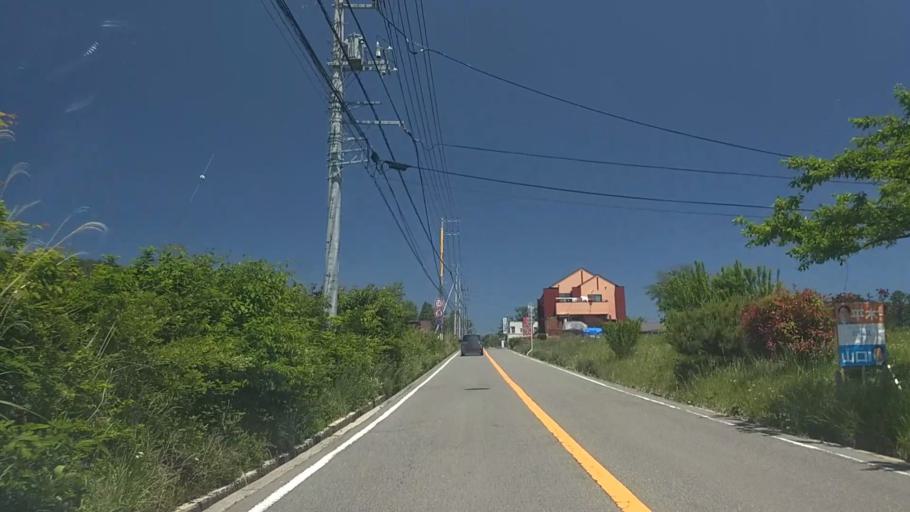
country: JP
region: Yamanashi
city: Nirasaki
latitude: 35.8466
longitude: 138.4328
